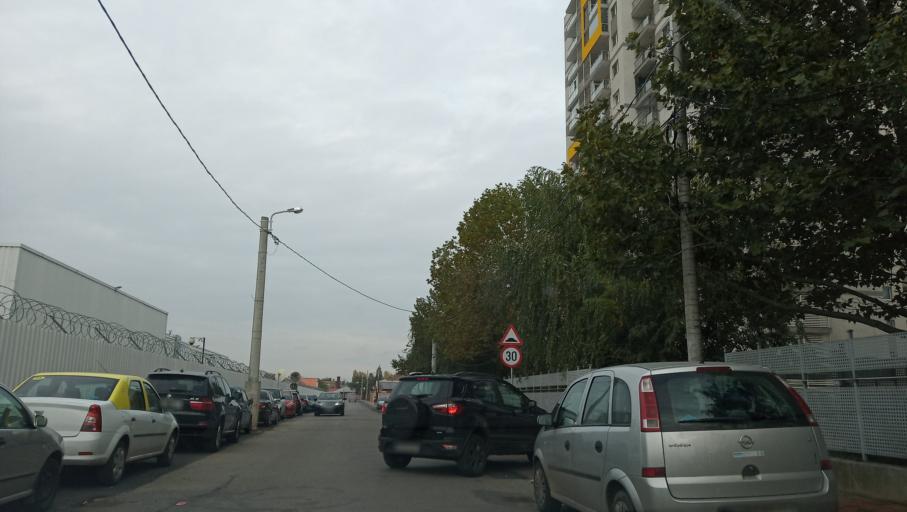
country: RO
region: Ilfov
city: Dobroesti
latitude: 44.4198
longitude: 26.1806
